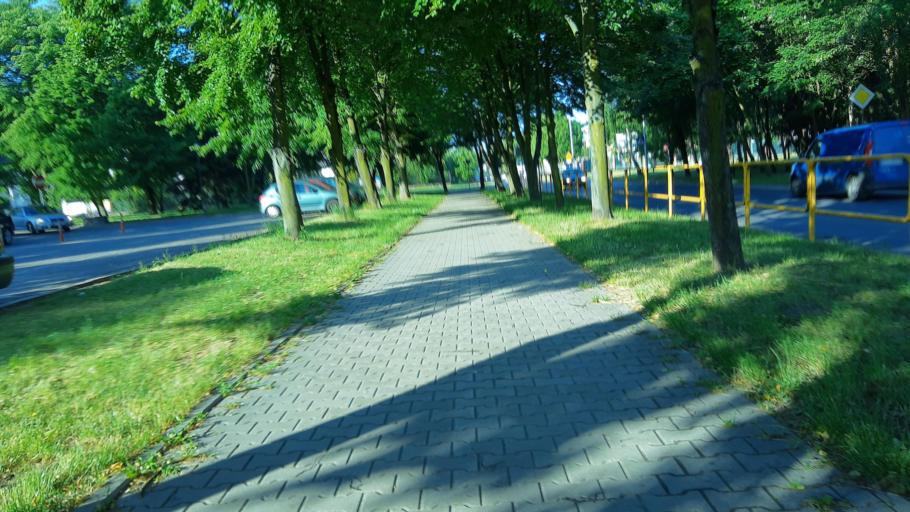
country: PL
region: Lodz Voivodeship
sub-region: Powiat sieradzki
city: Sieradz
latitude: 51.5825
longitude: 18.7092
